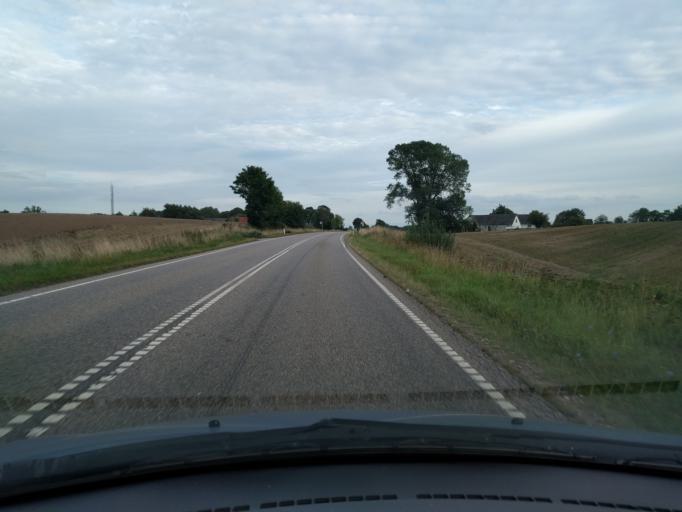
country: DK
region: Zealand
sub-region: Vordingborg Kommune
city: Nyrad
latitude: 55.0110
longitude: 11.9740
